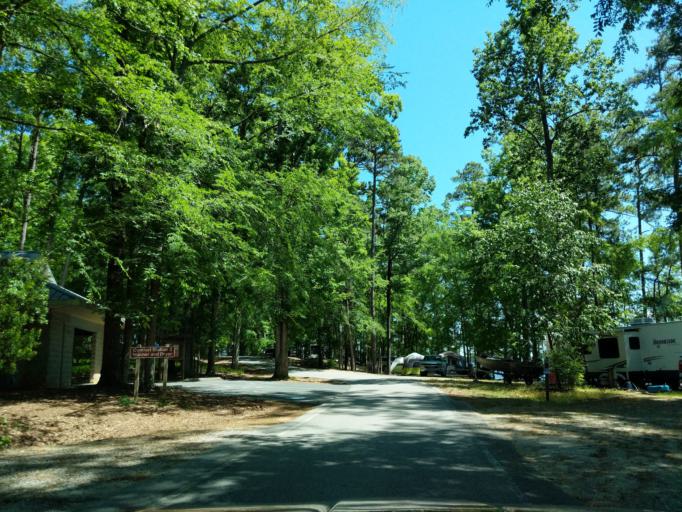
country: US
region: Georgia
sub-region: Columbia County
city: Appling
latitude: 33.6667
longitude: -82.3847
